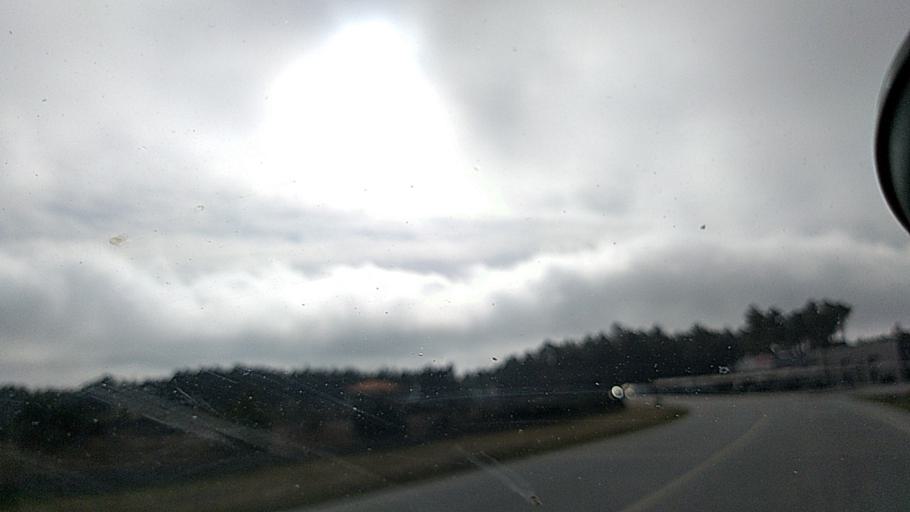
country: PT
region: Guarda
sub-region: Aguiar da Beira
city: Aguiar da Beira
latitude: 40.7965
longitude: -7.5197
